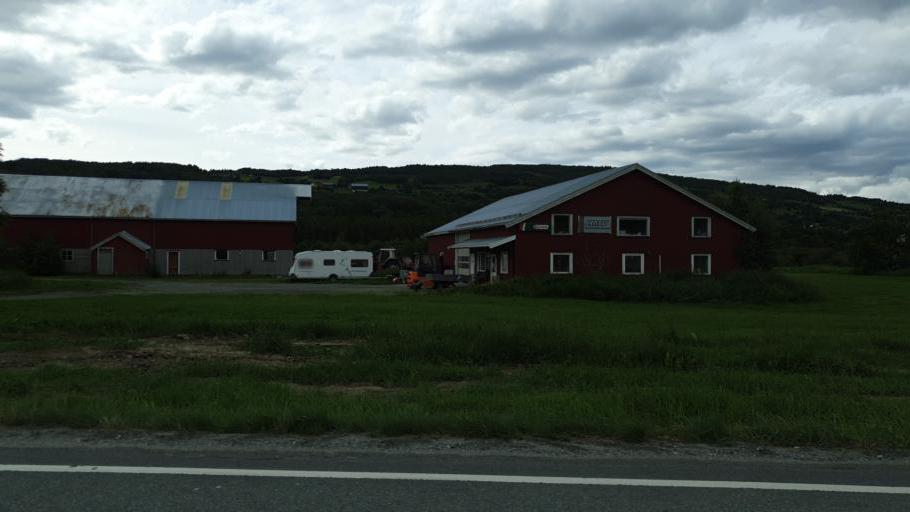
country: NO
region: Sor-Trondelag
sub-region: Oppdal
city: Oppdal
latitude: 62.5615
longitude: 9.6410
